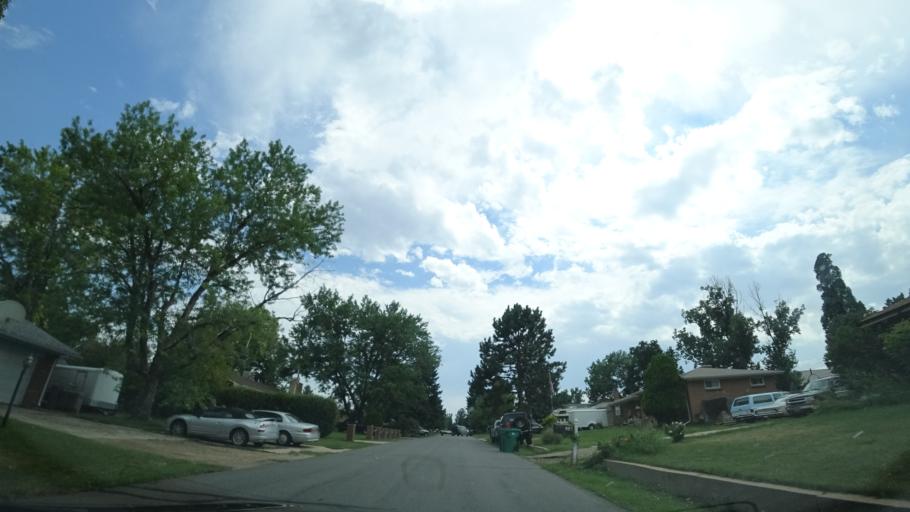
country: US
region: Colorado
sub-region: Jefferson County
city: Lakewood
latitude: 39.6987
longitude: -105.0793
